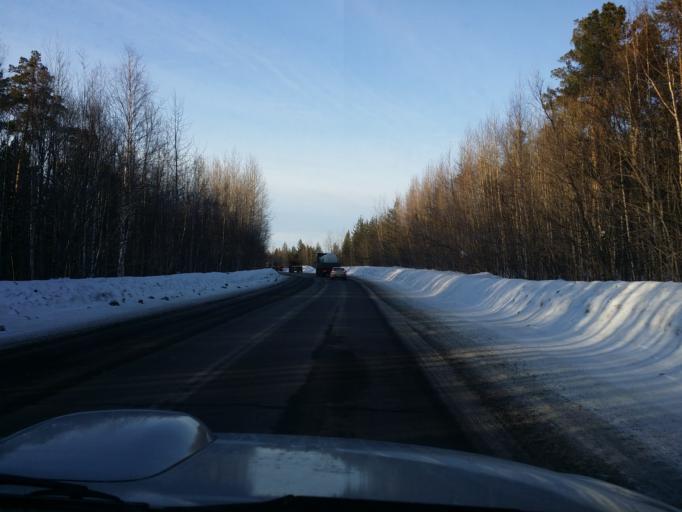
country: RU
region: Khanty-Mansiyskiy Avtonomnyy Okrug
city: Izluchinsk
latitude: 60.9595
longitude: 76.8510
